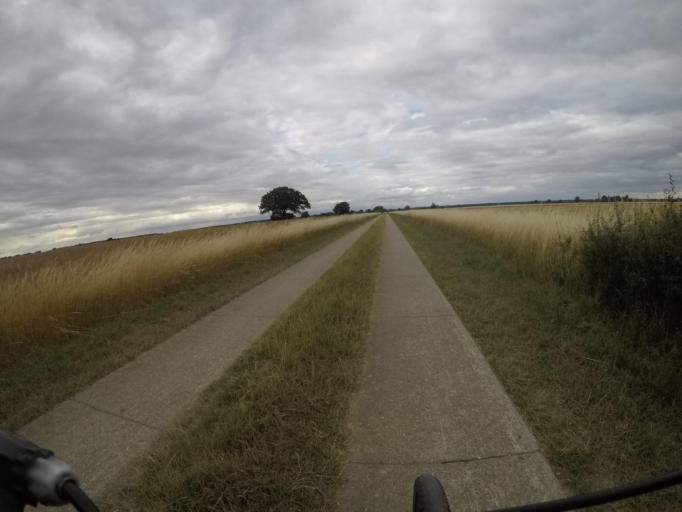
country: DE
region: Lower Saxony
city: Neu Darchau
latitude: 53.2431
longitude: 10.9120
